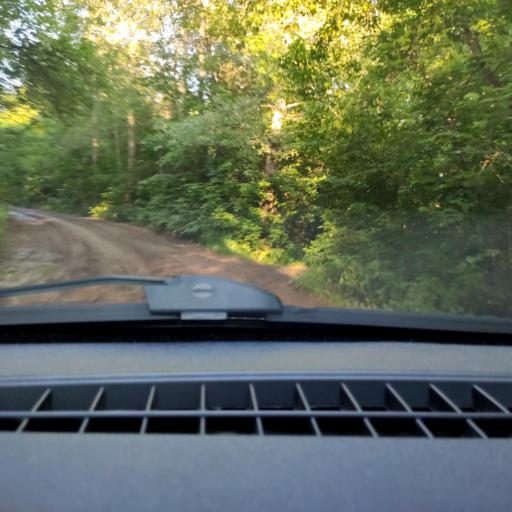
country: RU
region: Bashkortostan
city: Avdon
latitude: 54.6066
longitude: 55.6841
